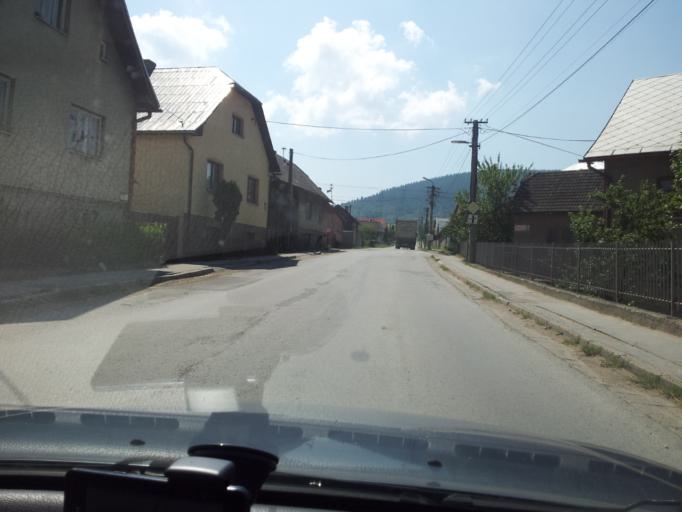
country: SK
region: Zilinsky
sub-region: Okres Dolny Kubin
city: Dolny Kubin
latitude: 49.3226
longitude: 19.3486
